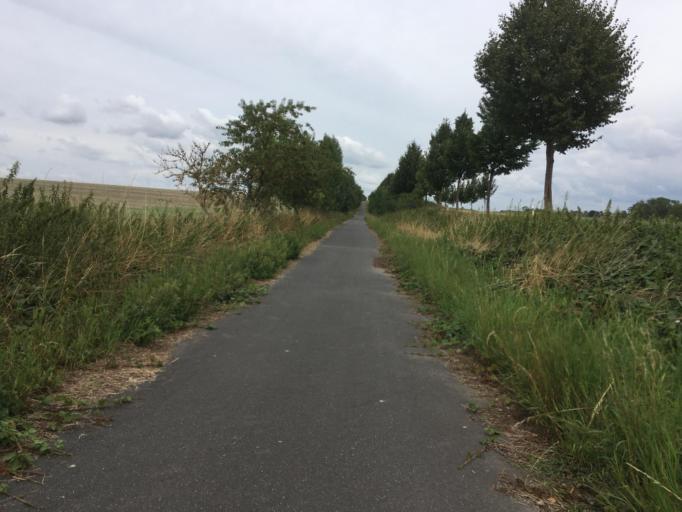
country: DE
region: Brandenburg
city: Prenzlau
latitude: 53.2492
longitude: 13.8420
